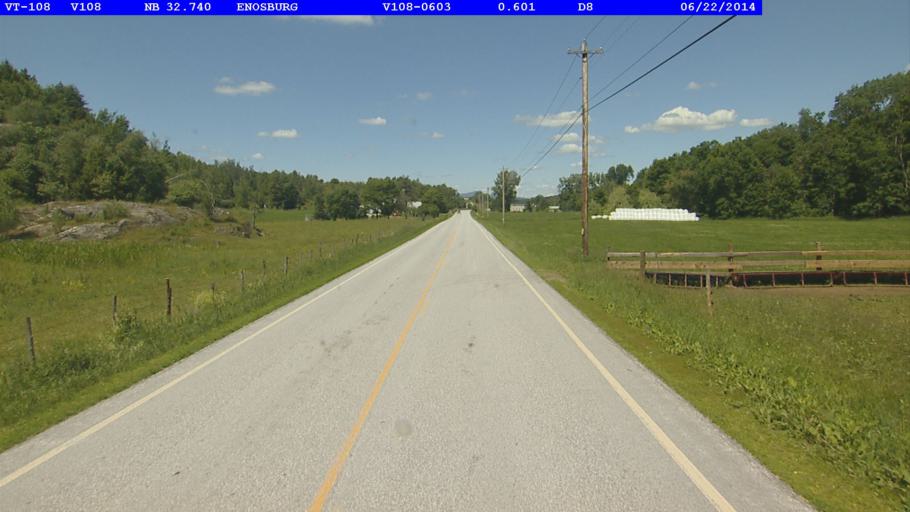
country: US
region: Vermont
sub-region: Franklin County
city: Enosburg Falls
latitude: 44.8469
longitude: -72.8061
